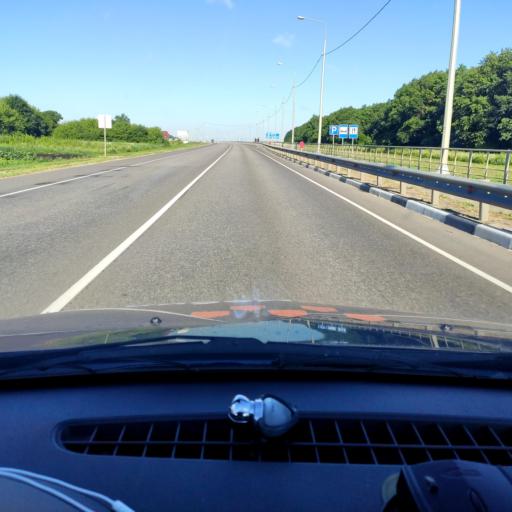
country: RU
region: Orjol
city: Pokrovskoye
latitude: 52.6222
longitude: 36.7817
